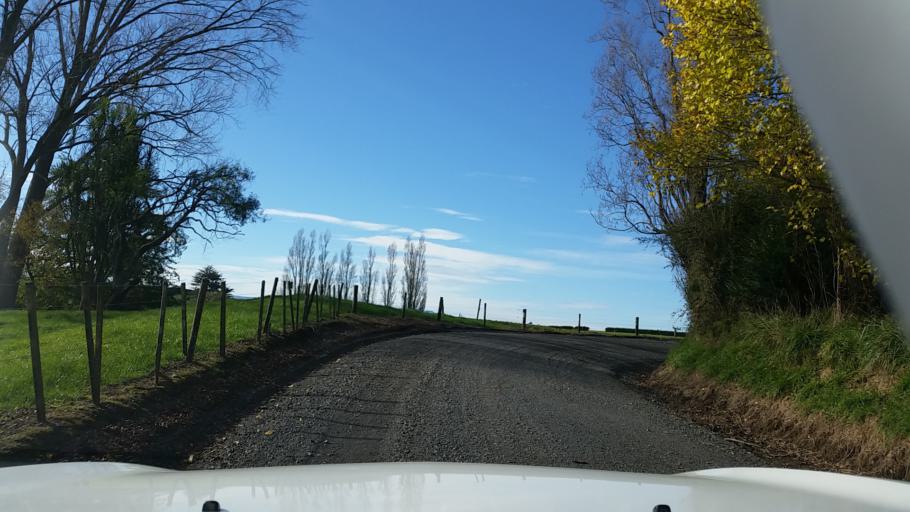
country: NZ
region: Waikato
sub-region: Matamata-Piako District
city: Matamata
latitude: -37.7941
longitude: 175.6344
